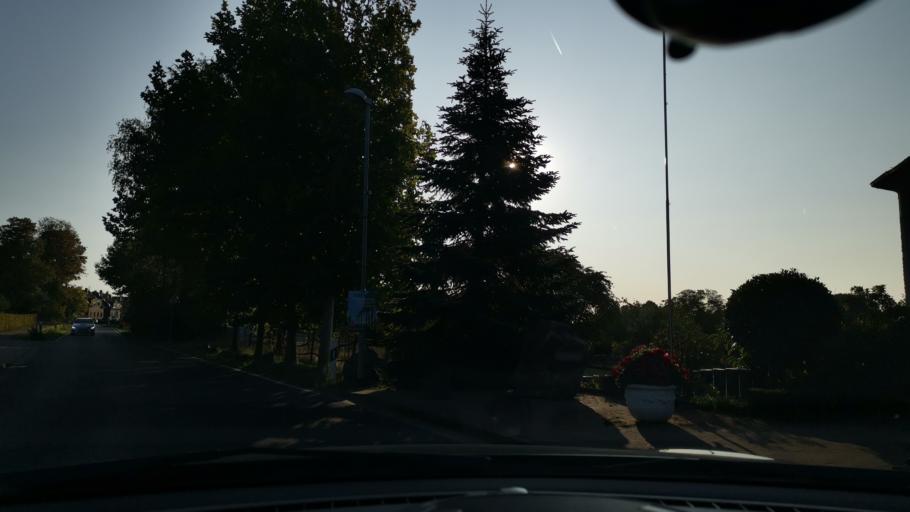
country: DE
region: North Rhine-Westphalia
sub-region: Regierungsbezirk Dusseldorf
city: Neubrueck
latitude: 51.0985
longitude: 6.6727
